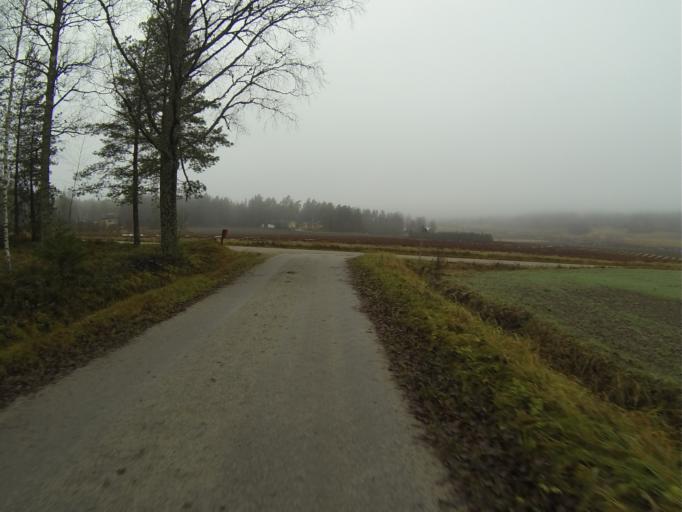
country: FI
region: Varsinais-Suomi
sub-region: Salo
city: Halikko
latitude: 60.4087
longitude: 22.9506
